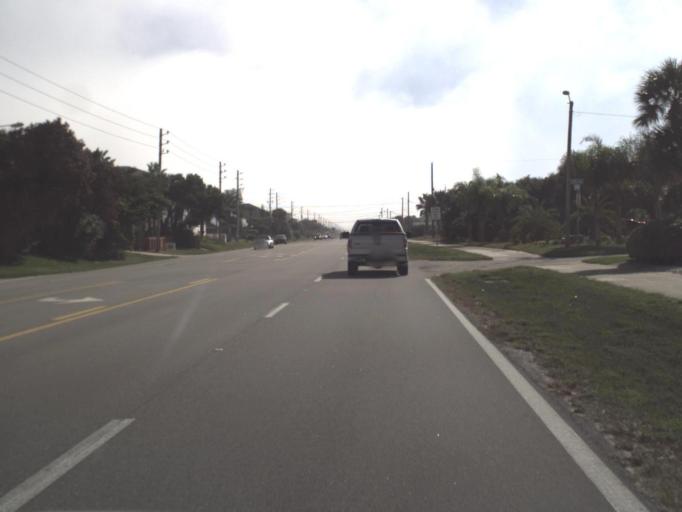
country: US
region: Florida
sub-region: Volusia County
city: Edgewater
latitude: 29.0212
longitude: -80.8870
